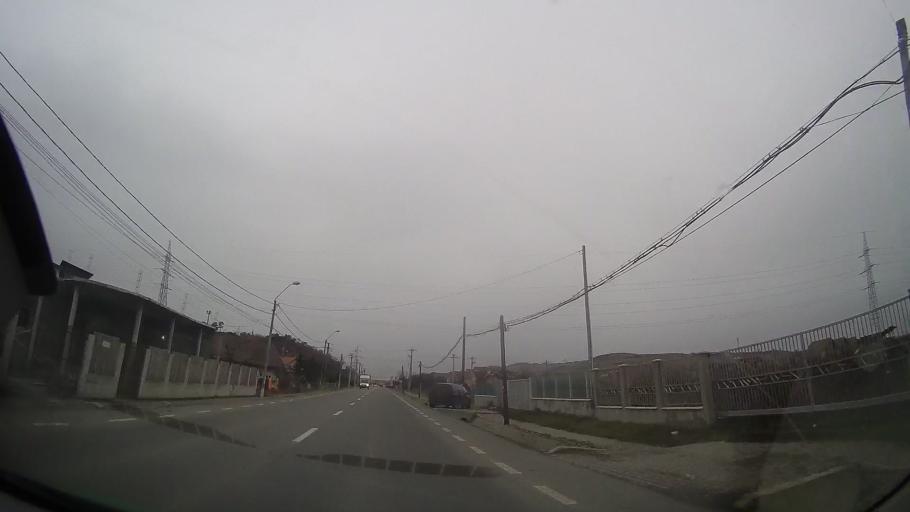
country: RO
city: Remetea
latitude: 46.5926
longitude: 24.5342
